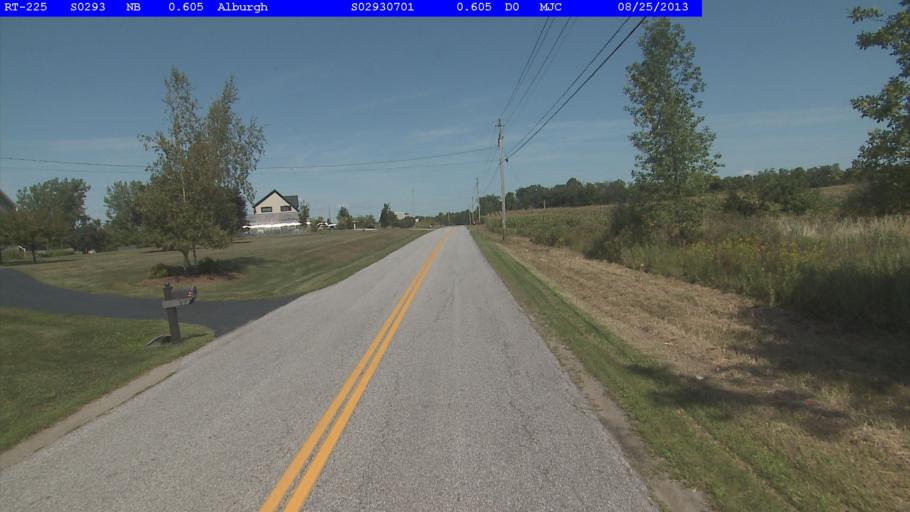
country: US
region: New York
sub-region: Clinton County
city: Rouses Point
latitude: 44.9974
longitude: -73.2961
